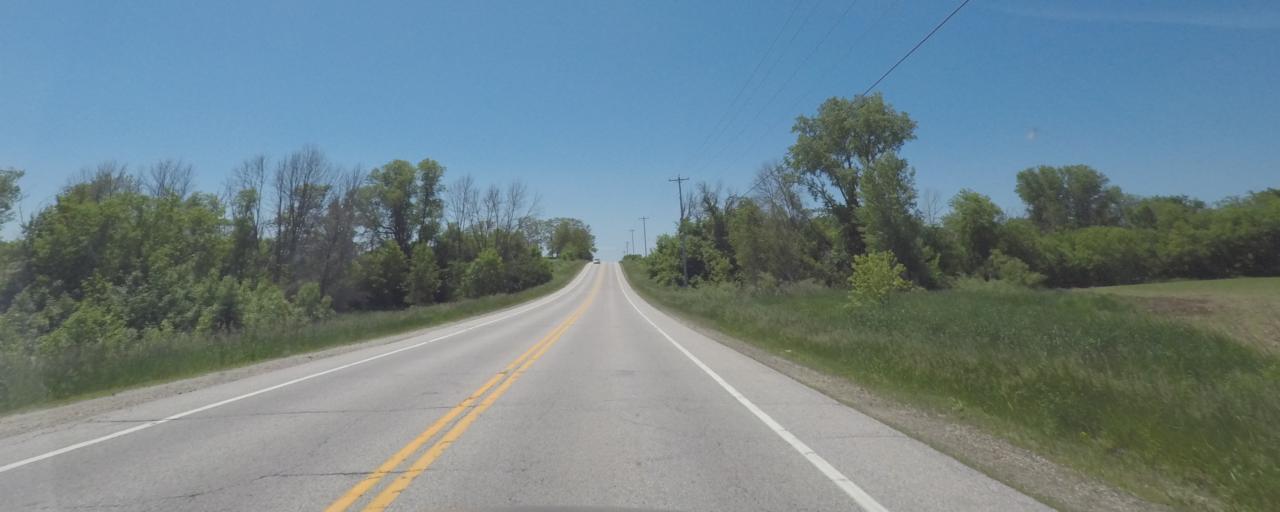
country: US
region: Wisconsin
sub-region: Ozaukee County
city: Kohler
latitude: 43.5787
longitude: -88.0566
